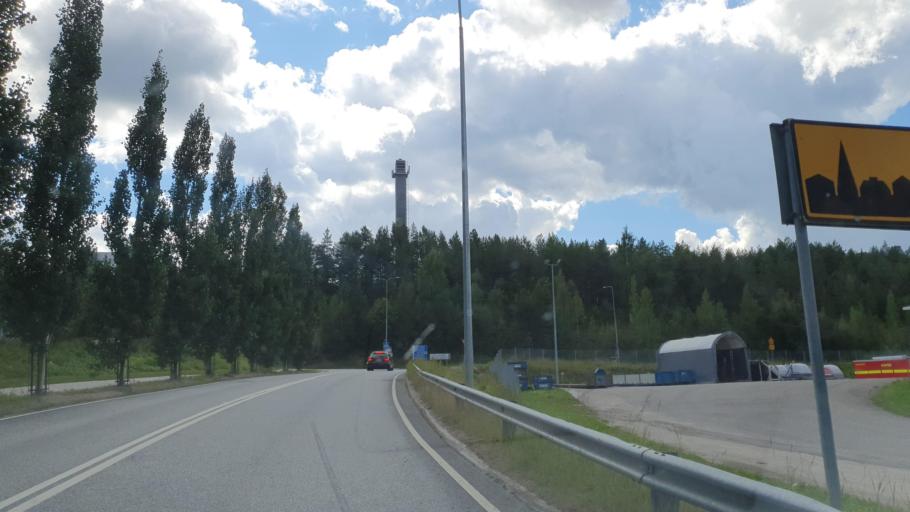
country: FI
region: Kainuu
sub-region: Kajaani
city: Kajaani
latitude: 64.2176
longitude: 27.7278
